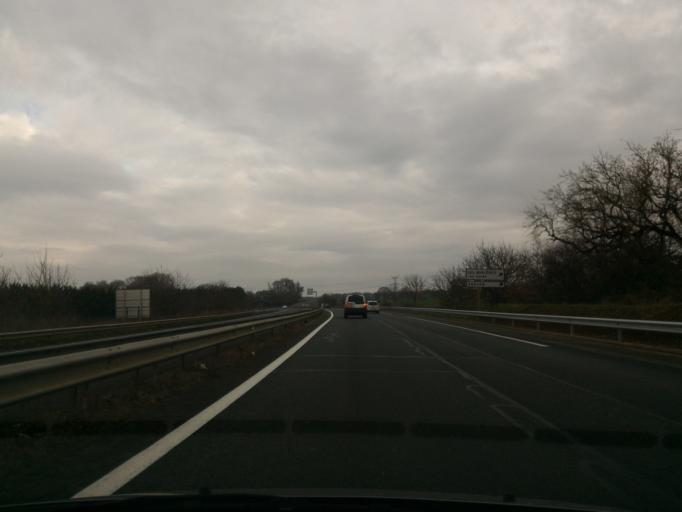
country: FR
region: Poitou-Charentes
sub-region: Departement de la Vienne
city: Celle-Levescault
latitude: 46.3648
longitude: 0.2059
